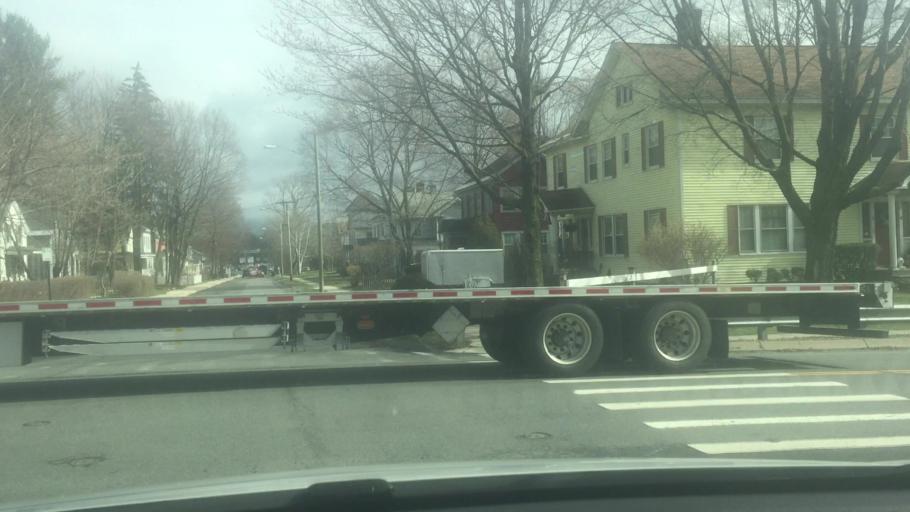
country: US
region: Massachusetts
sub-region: Berkshire County
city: Pittsfield
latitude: 42.4447
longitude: -73.2504
